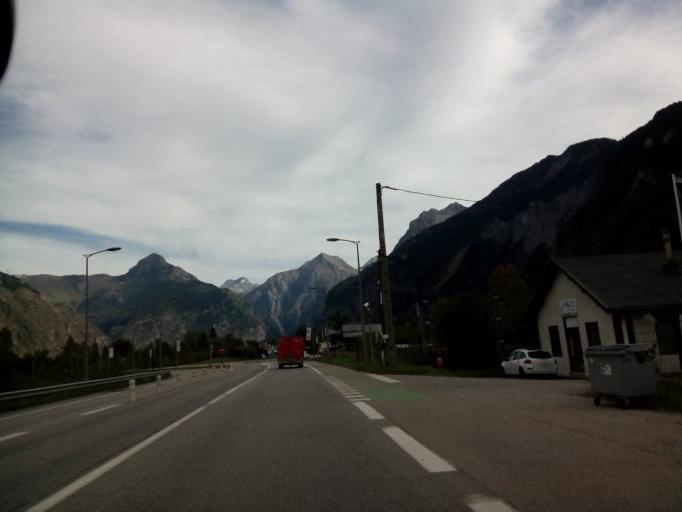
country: FR
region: Rhone-Alpes
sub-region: Departement de l'Isere
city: Huez
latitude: 45.0647
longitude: 6.0237
